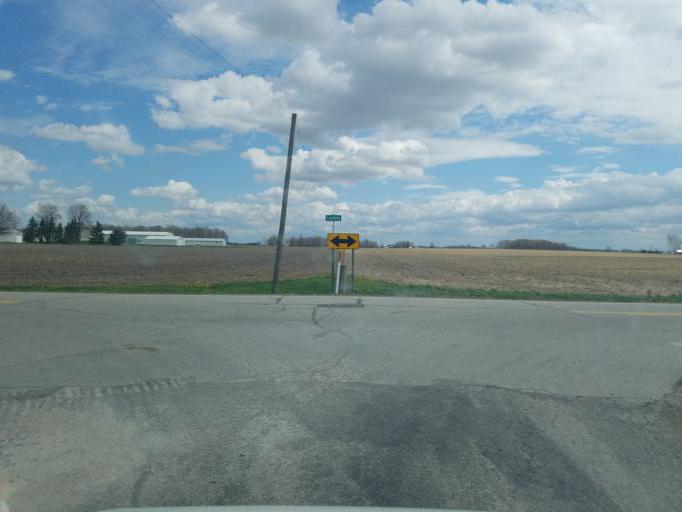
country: US
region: Ohio
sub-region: Crawford County
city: Bucyrus
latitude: 40.9218
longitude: -82.9018
